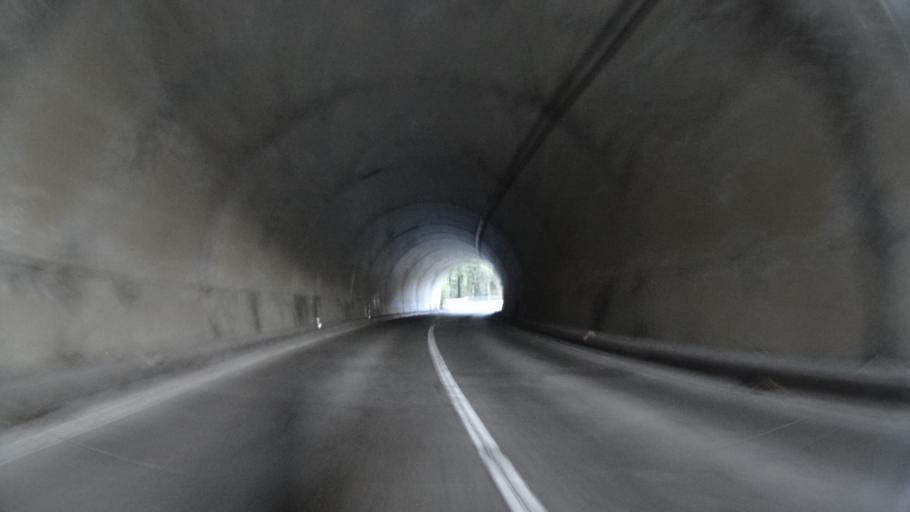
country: JP
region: Fukui
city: Maruoka
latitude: 36.1175
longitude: 136.3146
